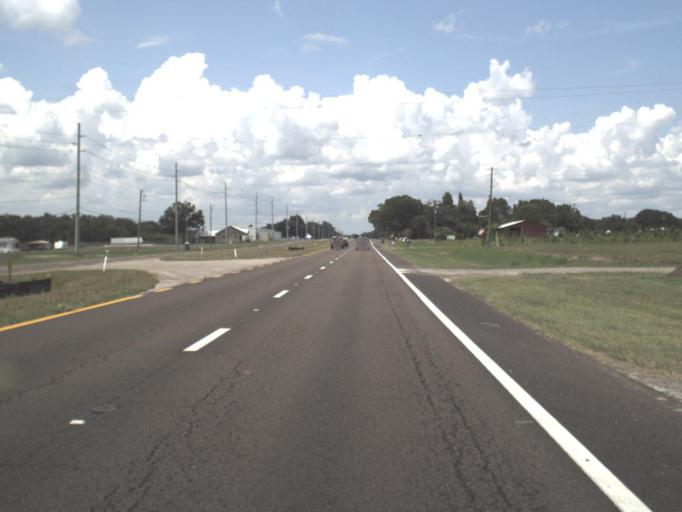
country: US
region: Florida
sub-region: Hillsborough County
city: Plant City
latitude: 27.9455
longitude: -82.1210
